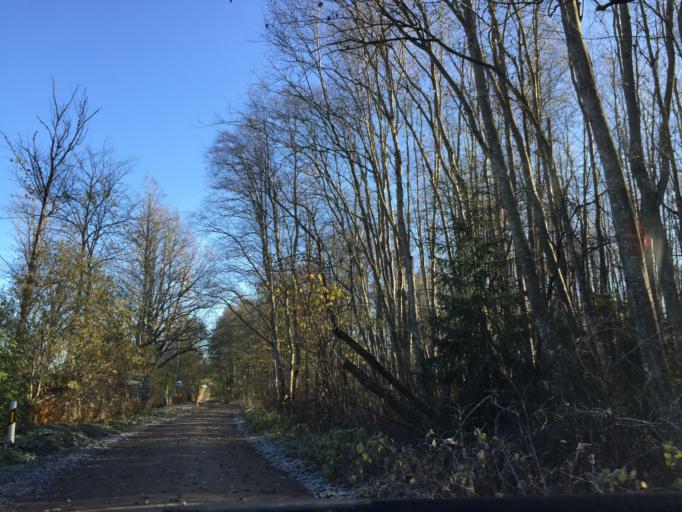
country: LV
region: Aizkraukles Rajons
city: Aizkraukle
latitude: 56.7055
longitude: 25.2886
